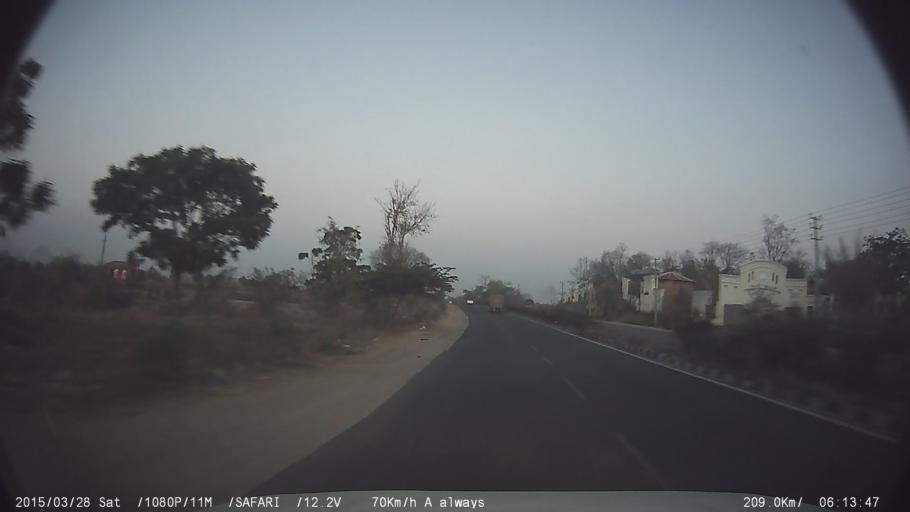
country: IN
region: Karnataka
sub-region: Ramanagara
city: Ramanagaram
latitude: 12.7704
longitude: 77.3495
